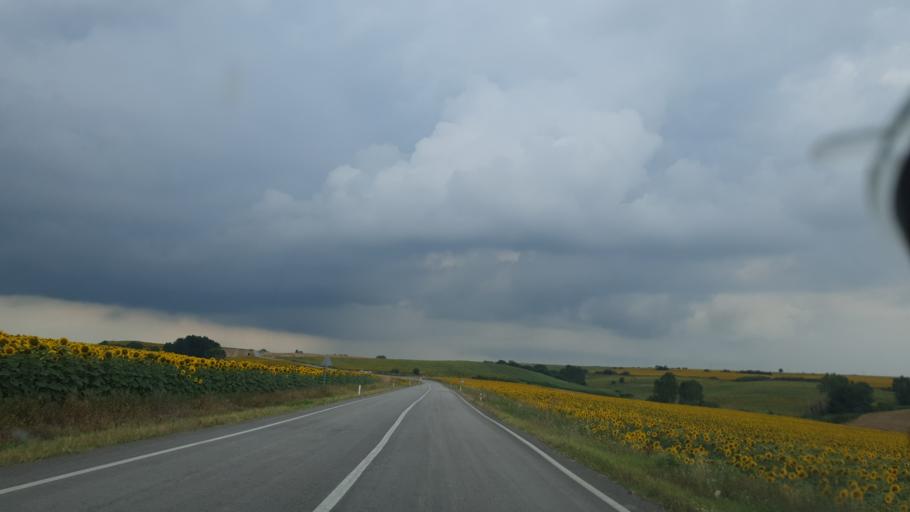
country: TR
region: Tekirdag
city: Hayrabolu
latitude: 41.2213
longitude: 27.0043
